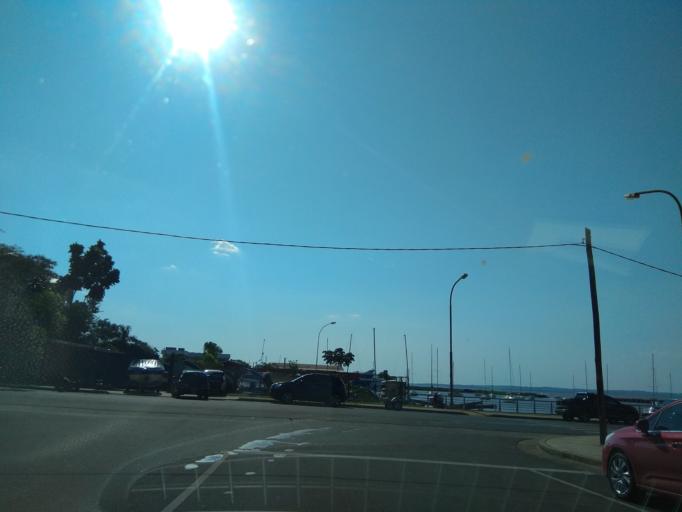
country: AR
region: Misiones
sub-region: Departamento de Capital
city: Posadas
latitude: -27.3546
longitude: -55.9108
